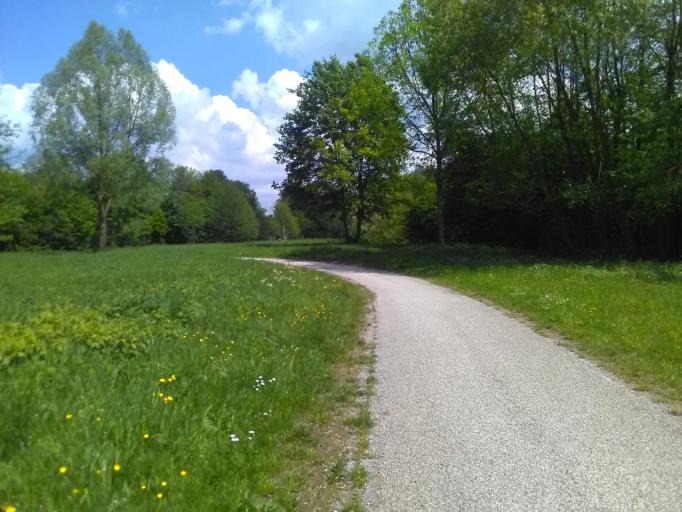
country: DE
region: Bavaria
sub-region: Upper Franconia
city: Kronach
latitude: 50.2257
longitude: 11.3148
